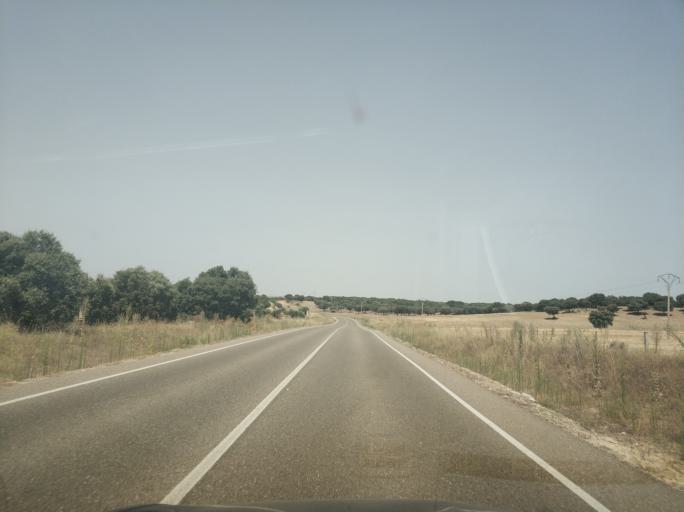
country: ES
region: Castille and Leon
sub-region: Provincia de Salamanca
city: Florida de Liebana
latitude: 41.0360
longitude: -5.7363
